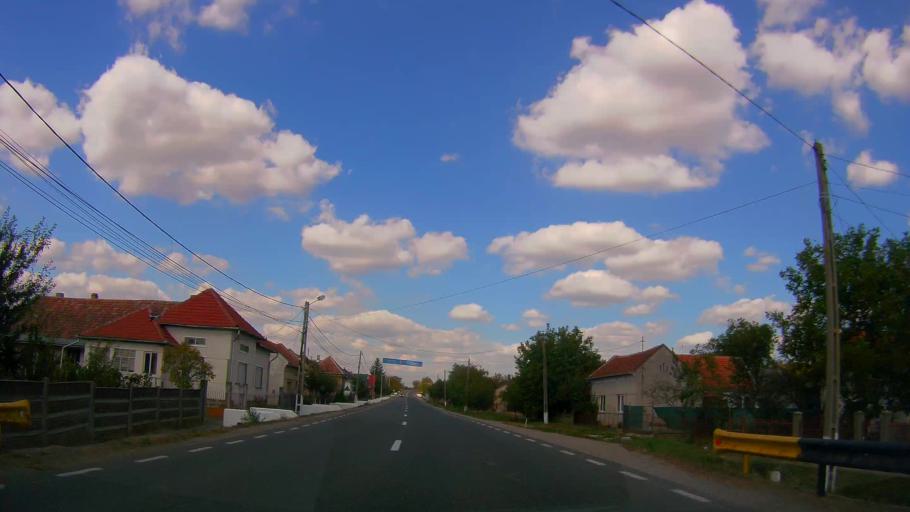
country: RO
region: Satu Mare
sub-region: Comuna Beltiug
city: Beltiug
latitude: 47.5522
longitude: 22.8453
